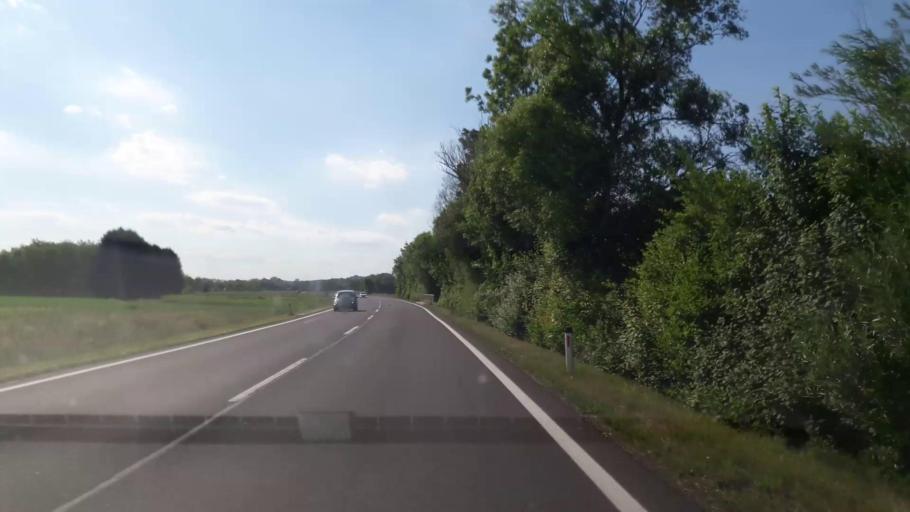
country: AT
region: Styria
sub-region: Politischer Bezirk Suedoststeiermark
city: Fehring
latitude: 46.9413
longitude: 16.0288
